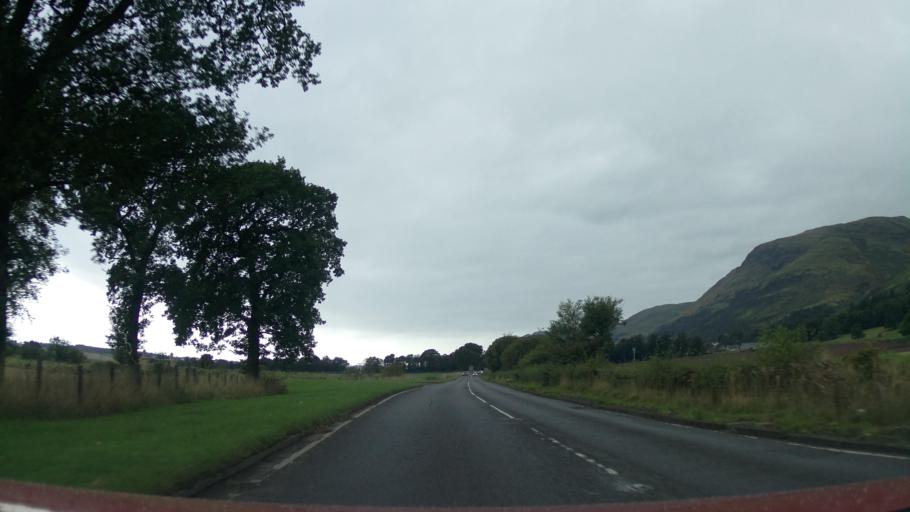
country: GB
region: Scotland
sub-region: Clackmannanshire
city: Alva
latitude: 56.1525
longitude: -3.7738
